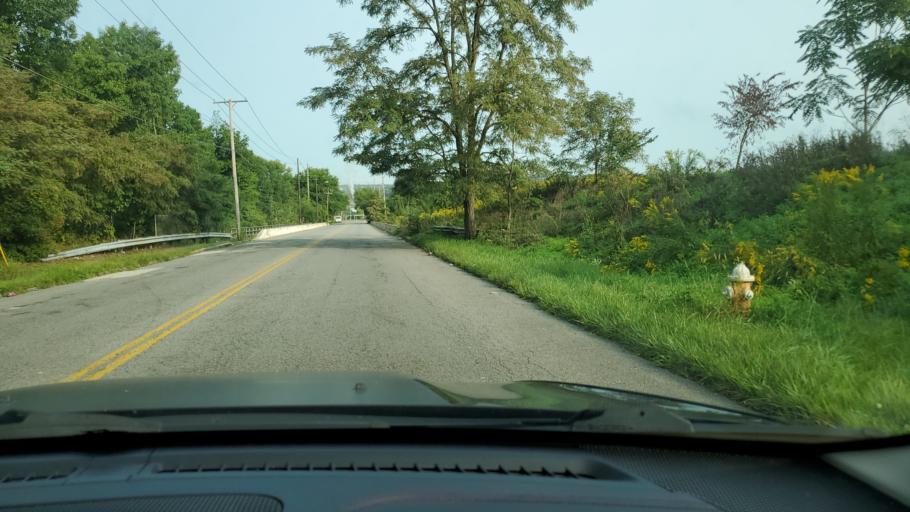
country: US
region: Ohio
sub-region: Mahoning County
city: Campbell
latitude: 41.0727
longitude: -80.6218
